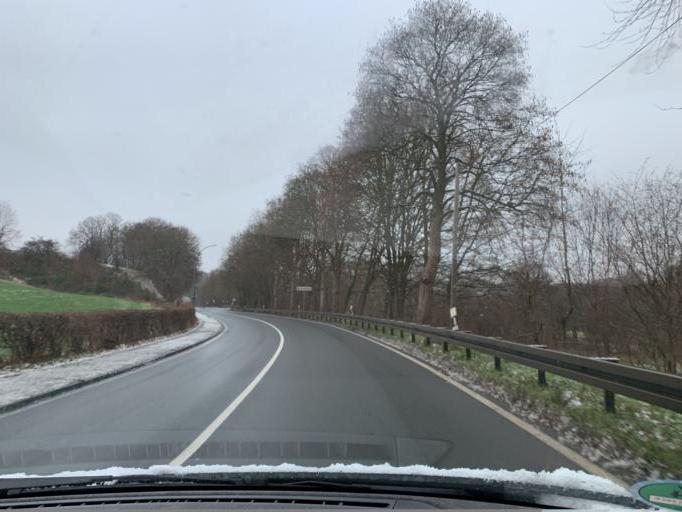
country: DE
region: North Rhine-Westphalia
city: Stolberg
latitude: 50.7373
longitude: 6.1754
